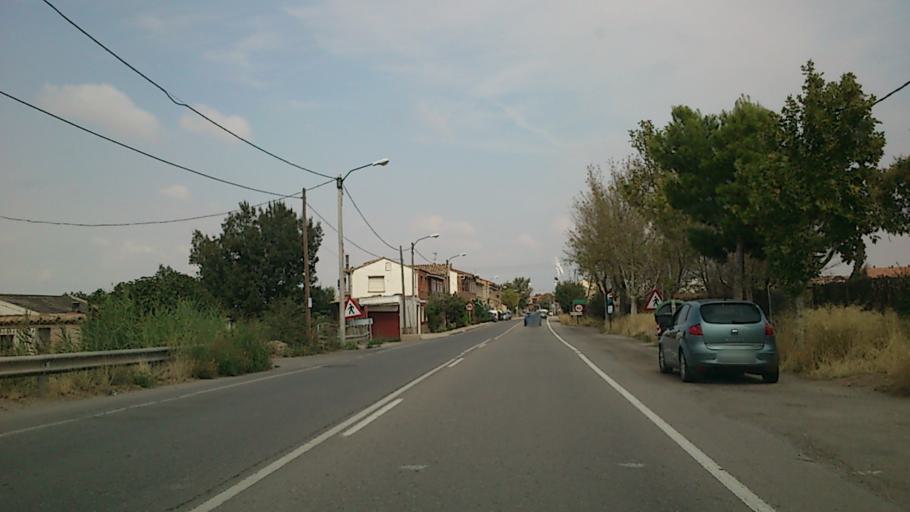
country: ES
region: Aragon
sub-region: Provincia de Zaragoza
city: Zaragoza
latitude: 41.6789
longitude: -0.8299
